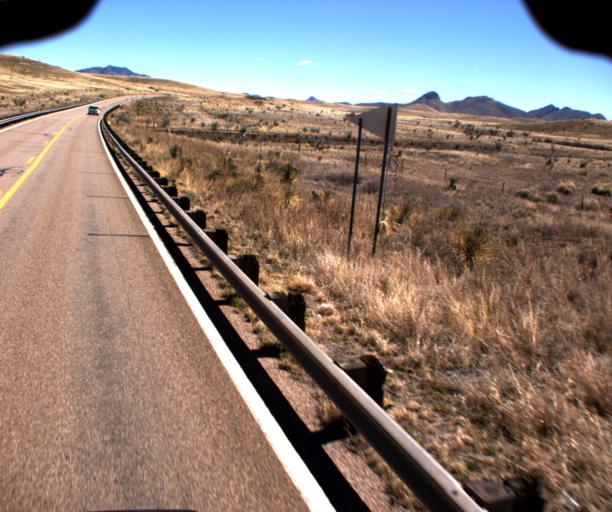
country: US
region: Arizona
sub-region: Cochise County
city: Huachuca City
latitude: 31.7085
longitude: -110.5773
